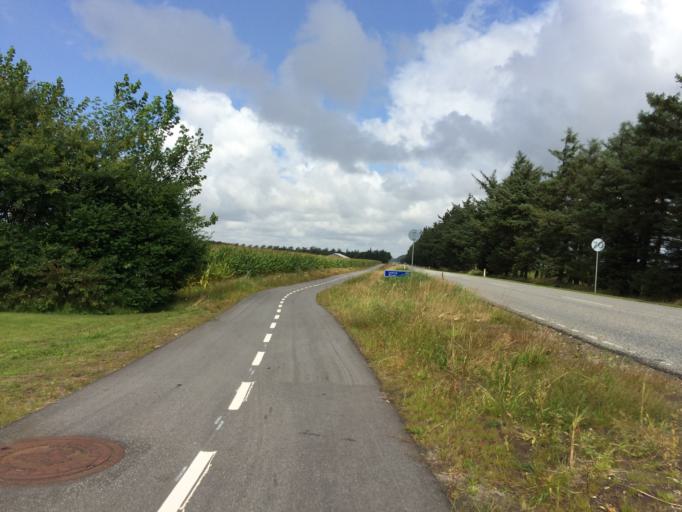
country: DK
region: Central Jutland
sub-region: Holstebro Kommune
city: Ulfborg
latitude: 56.3026
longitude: 8.3387
